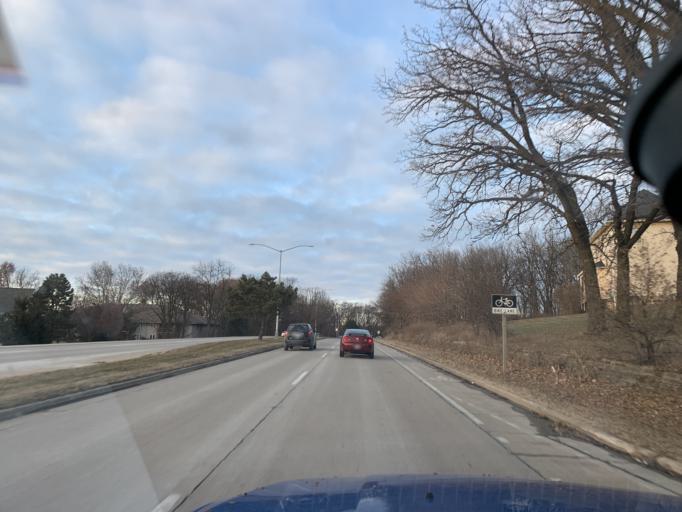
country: US
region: Wisconsin
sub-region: Dane County
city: Fitchburg
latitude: 43.0083
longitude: -89.4281
